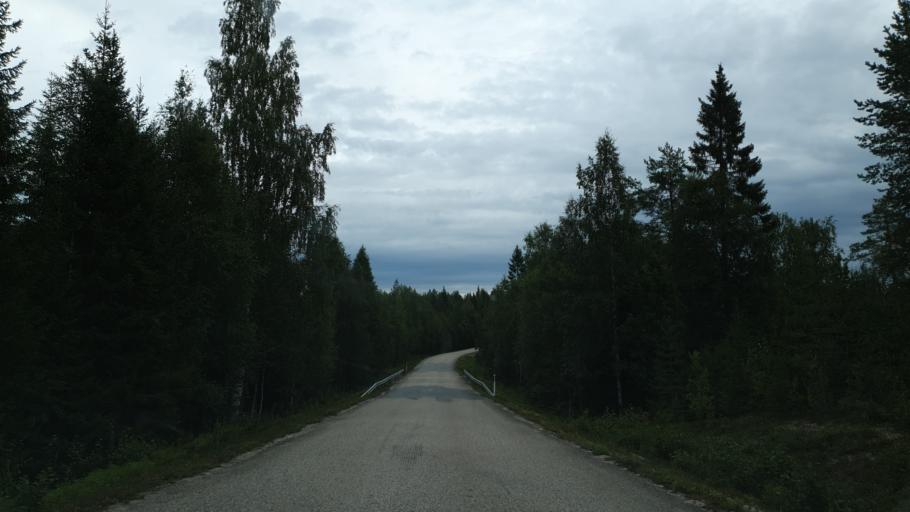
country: FI
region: Kainuu
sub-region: Kehys-Kainuu
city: Kuhmo
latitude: 64.3516
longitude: 29.1499
